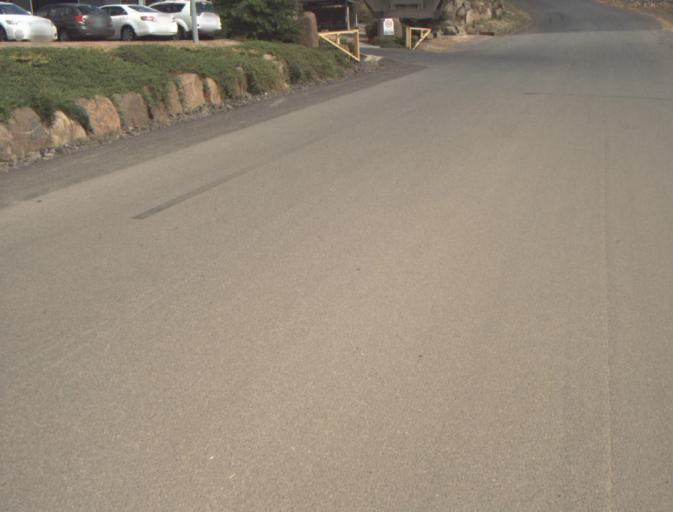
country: AU
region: Tasmania
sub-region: Launceston
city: Summerhill
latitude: -41.4795
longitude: 147.1543
